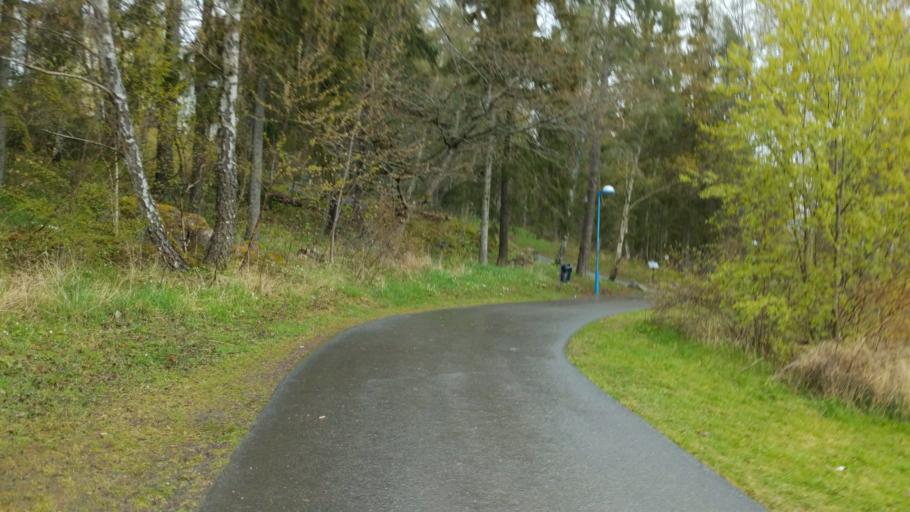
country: SE
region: Stockholm
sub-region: Stockholms Kommun
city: Kista
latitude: 59.3902
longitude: 17.8955
